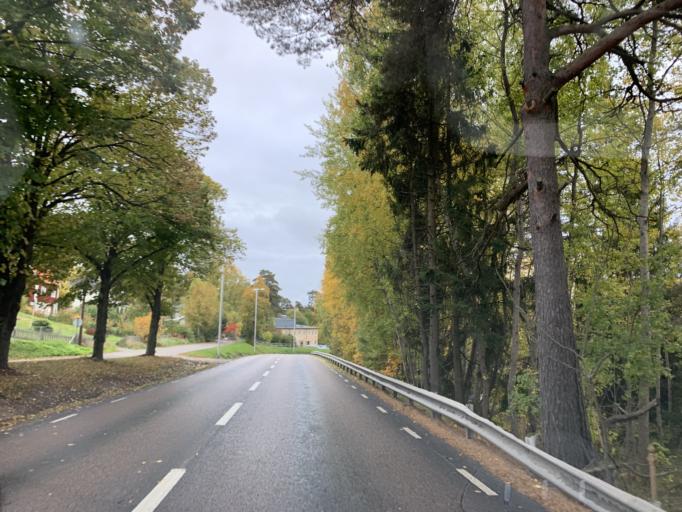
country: SE
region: Stockholm
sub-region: Botkyrka Kommun
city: Varsta
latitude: 59.1679
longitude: 17.7978
